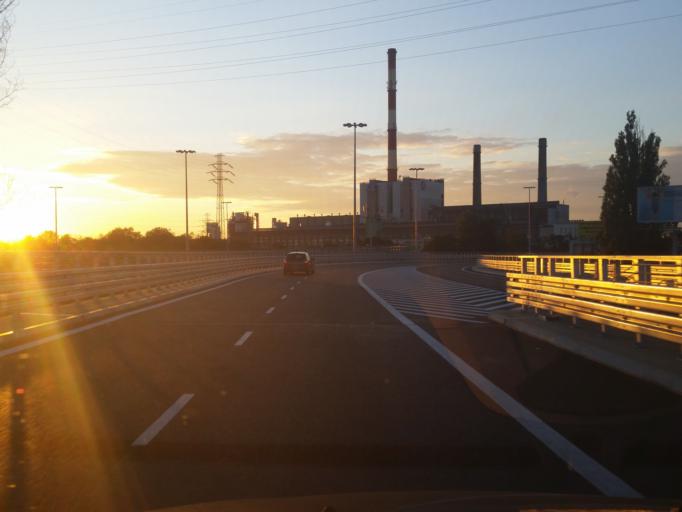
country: PL
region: Masovian Voivodeship
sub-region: Warszawa
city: Zoliborz
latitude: 52.2918
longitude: 21.0028
